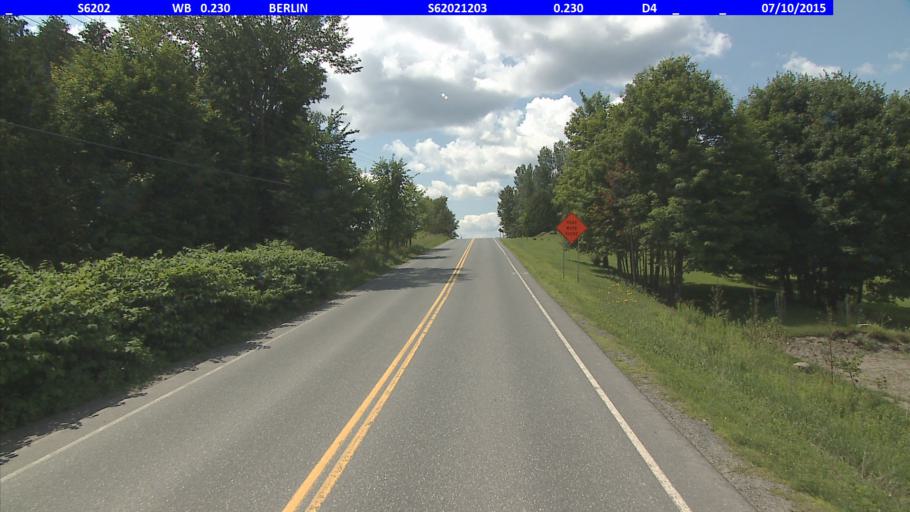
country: US
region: Vermont
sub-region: Washington County
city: South Barre
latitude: 44.1918
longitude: -72.5514
